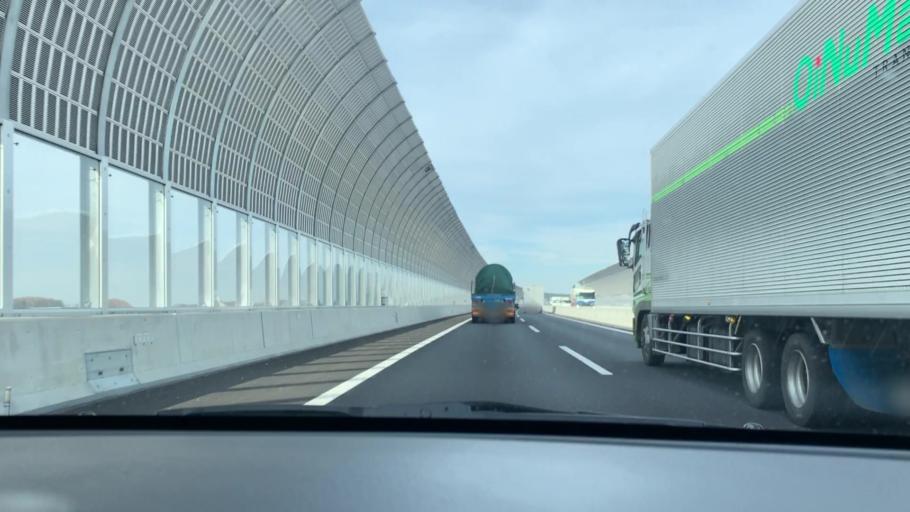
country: JP
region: Chiba
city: Matsudo
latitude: 35.7853
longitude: 139.8818
